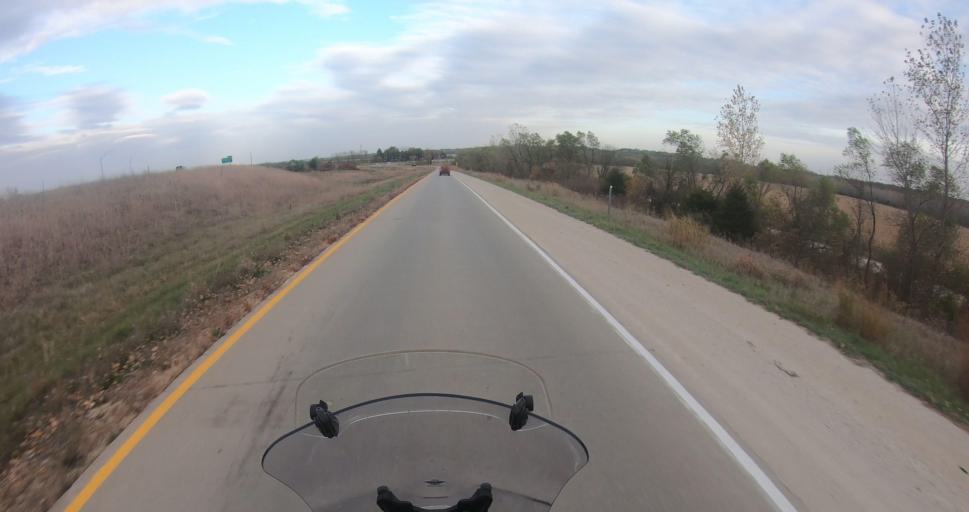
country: US
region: Iowa
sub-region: Warren County
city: Carlisle
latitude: 41.5107
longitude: -93.5274
